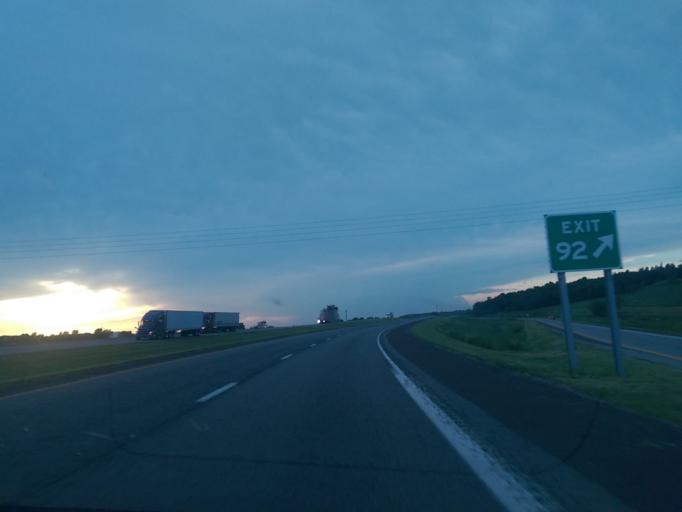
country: US
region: Missouri
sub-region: Holt County
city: Mound City
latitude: 40.1908
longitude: -95.3571
